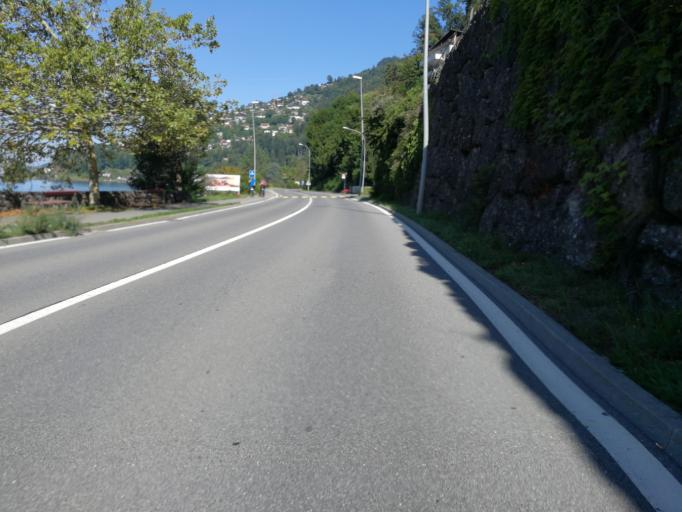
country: CH
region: Lucerne
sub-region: Lucerne-Land District
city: Vitznau
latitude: 47.0200
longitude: 8.4705
